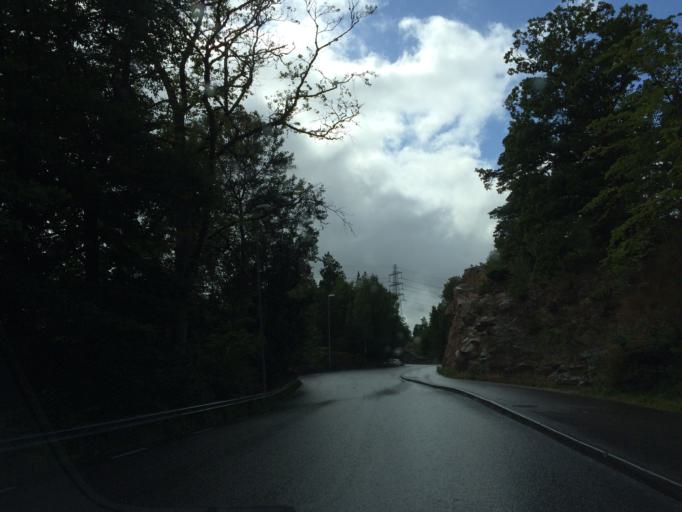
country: SE
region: Vaestra Goetaland
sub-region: Trollhattan
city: Trollhattan
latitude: 58.2789
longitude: 12.2735
